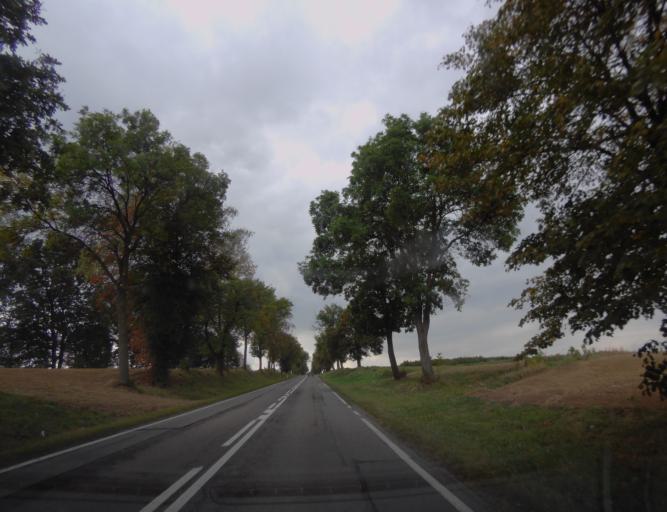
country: PL
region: Lublin Voivodeship
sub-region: Powiat krasnostawski
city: Zolkiewka
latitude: 50.9255
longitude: 22.8942
